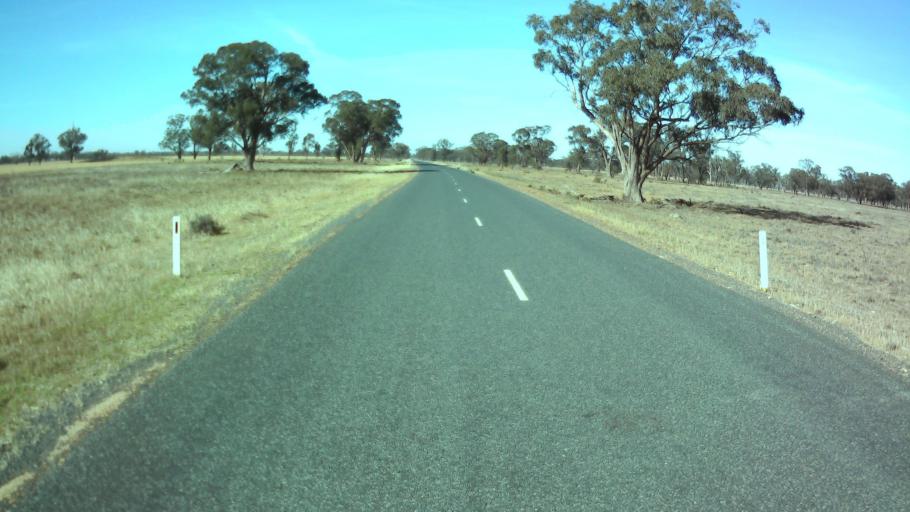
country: AU
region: New South Wales
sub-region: Weddin
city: Grenfell
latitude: -34.0788
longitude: 147.8975
